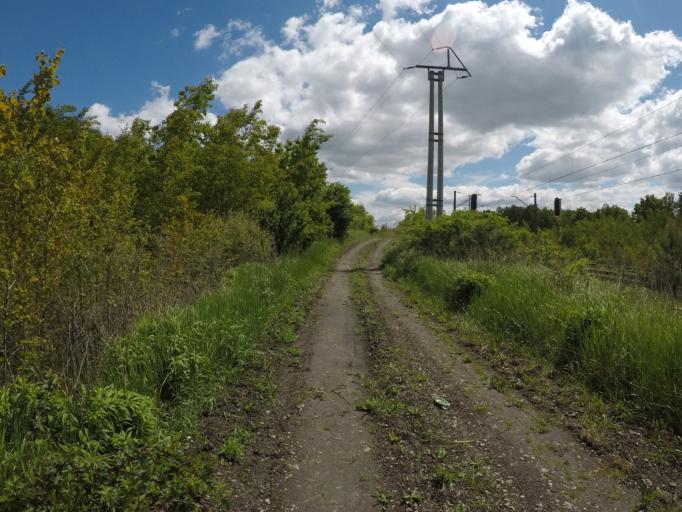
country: PL
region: Swietokrzyskie
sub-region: Powiat kielecki
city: Kostomloty Pierwsze
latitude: 50.9269
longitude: 20.6052
